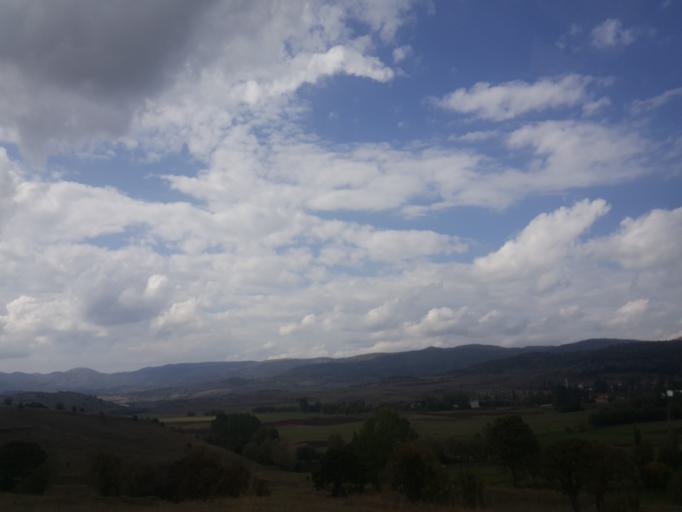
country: TR
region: Tokat
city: Bereketli
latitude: 40.5342
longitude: 37.2950
